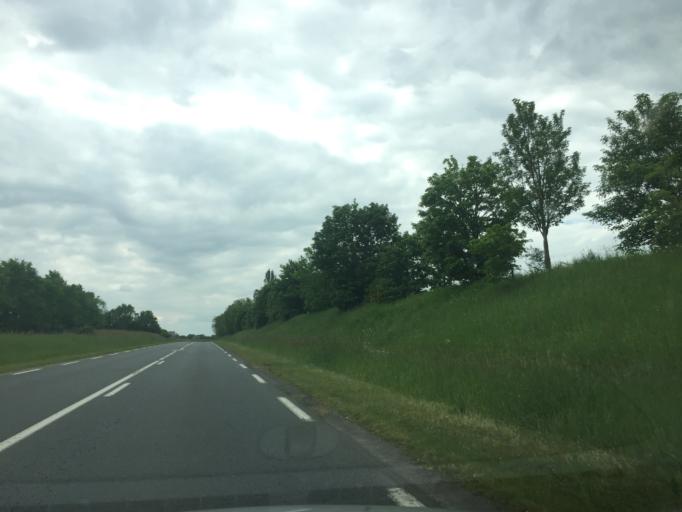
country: FR
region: Poitou-Charentes
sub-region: Departement de la Vienne
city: Lusignan
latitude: 46.4408
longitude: 0.1391
